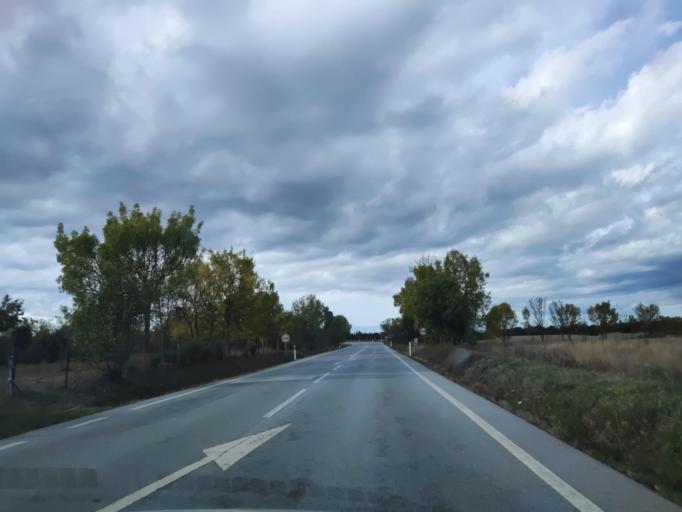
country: ES
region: Castille and Leon
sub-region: Provincia de Salamanca
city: Aldea del Obispo
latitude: 40.6801
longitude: -6.8684
